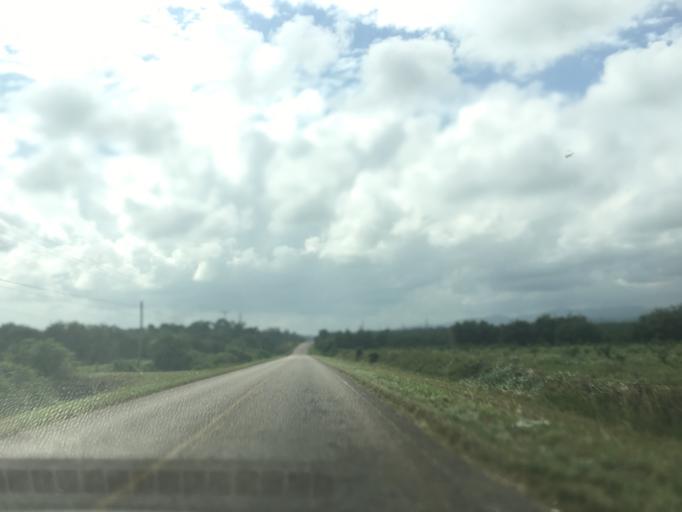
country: BZ
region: Stann Creek
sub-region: Dangriga
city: Dangriga
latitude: 16.9746
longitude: -88.3001
